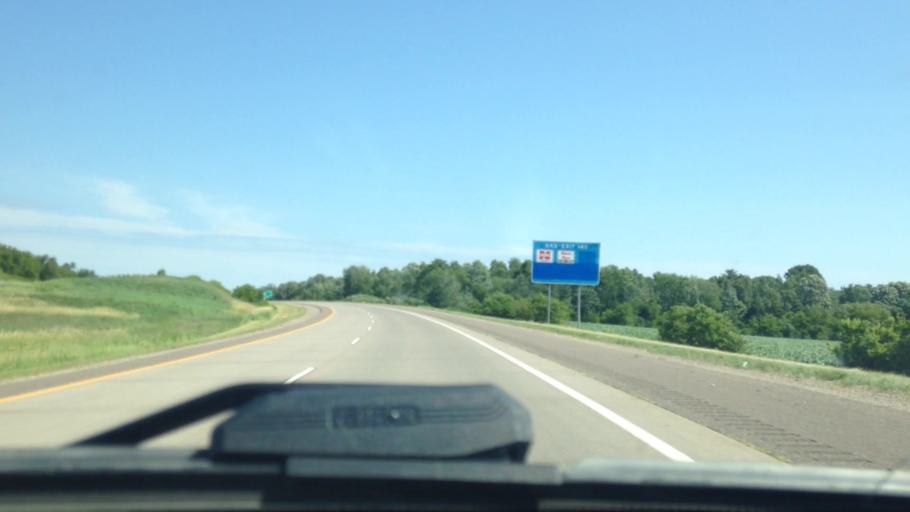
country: US
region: Wisconsin
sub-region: Barron County
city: Rice Lake
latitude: 45.4641
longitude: -91.7572
